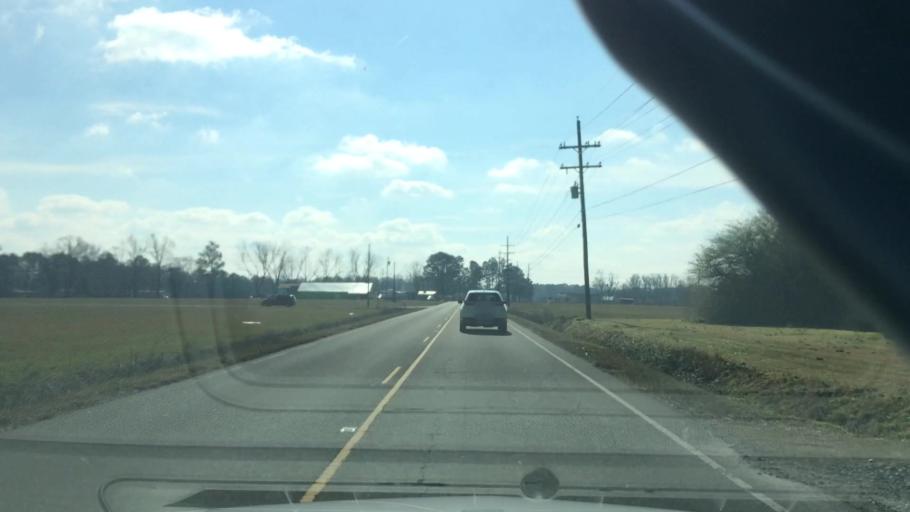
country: US
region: North Carolina
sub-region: Duplin County
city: Beulaville
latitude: 34.8899
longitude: -77.7837
